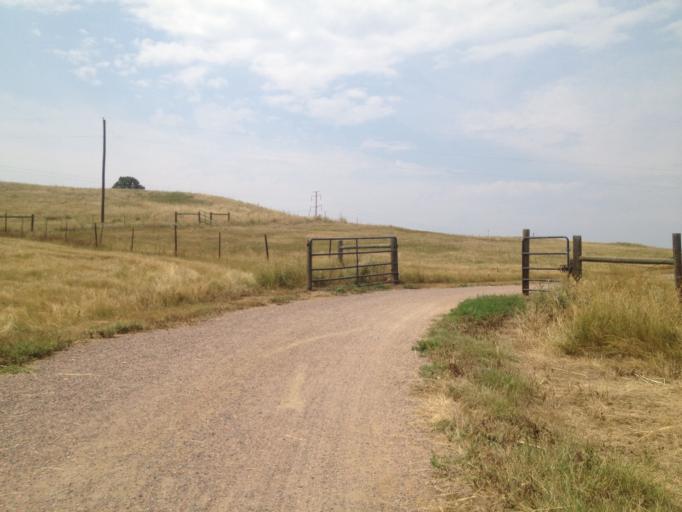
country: US
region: Colorado
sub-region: Boulder County
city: Superior
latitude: 39.9504
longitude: -105.1793
